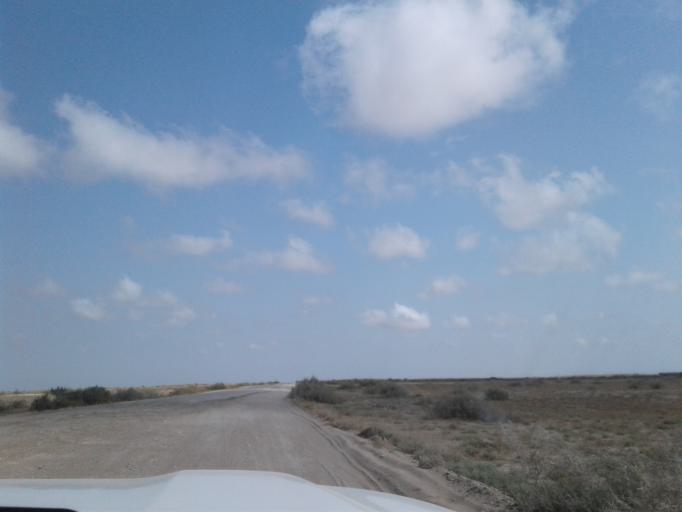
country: IR
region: Golestan
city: Gomishan
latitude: 37.6289
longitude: 53.9286
